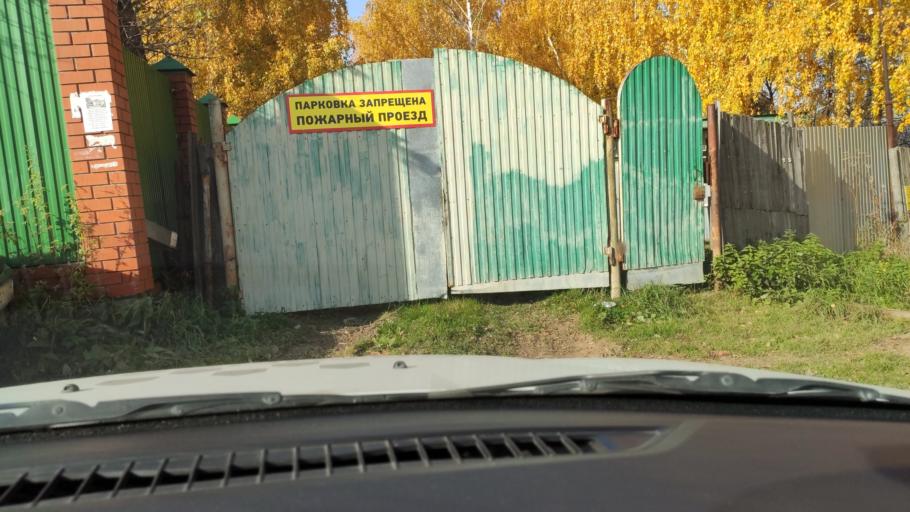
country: RU
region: Perm
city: Sylva
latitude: 58.0483
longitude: 56.7348
